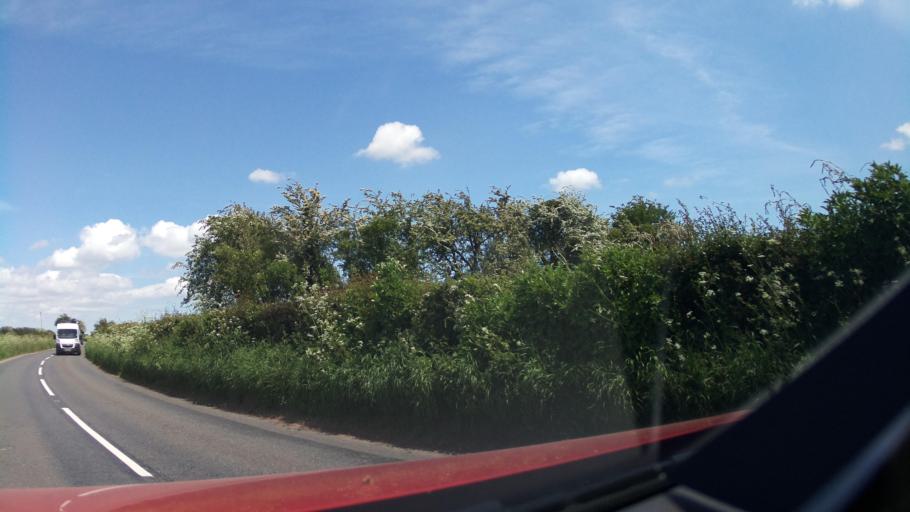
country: GB
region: Wales
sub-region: Monmouthshire
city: Mitchel Troy
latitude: 51.7281
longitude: -2.7540
